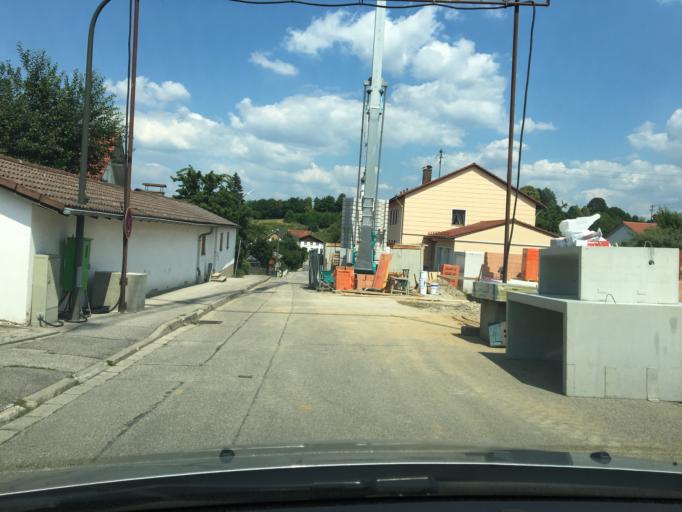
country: DE
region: Bavaria
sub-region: Upper Bavaria
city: Neumarkt-Sankt Veit
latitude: 48.3573
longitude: 12.5093
